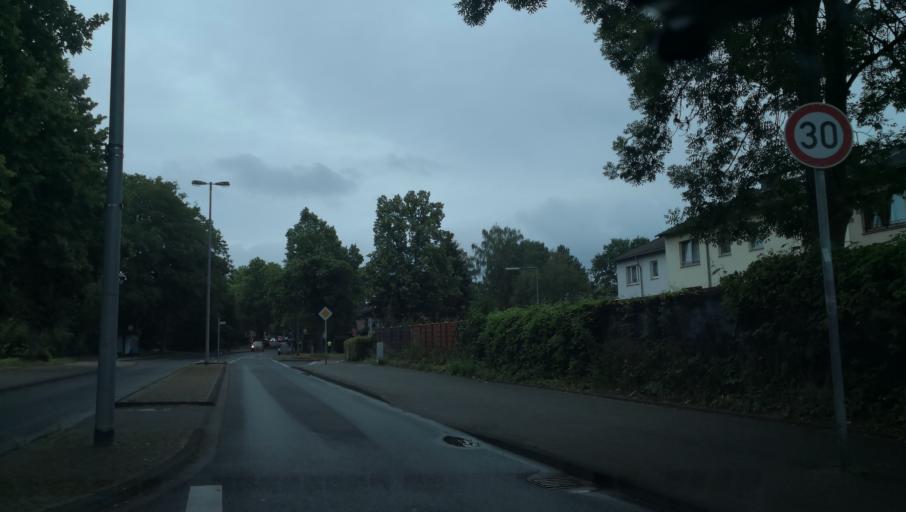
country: DE
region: North Rhine-Westphalia
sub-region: Regierungsbezirk Koln
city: Mengenich
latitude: 50.9689
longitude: 6.8948
